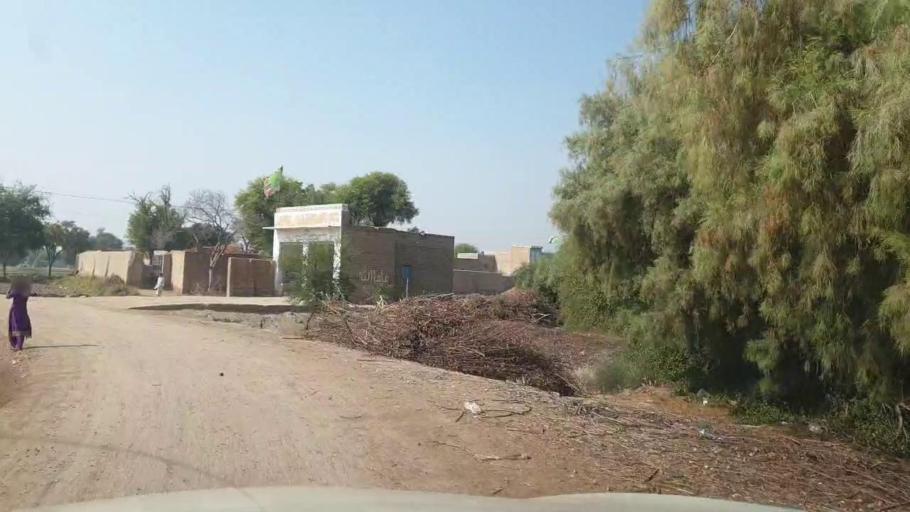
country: PK
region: Sindh
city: Bhan
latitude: 26.5154
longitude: 67.7729
